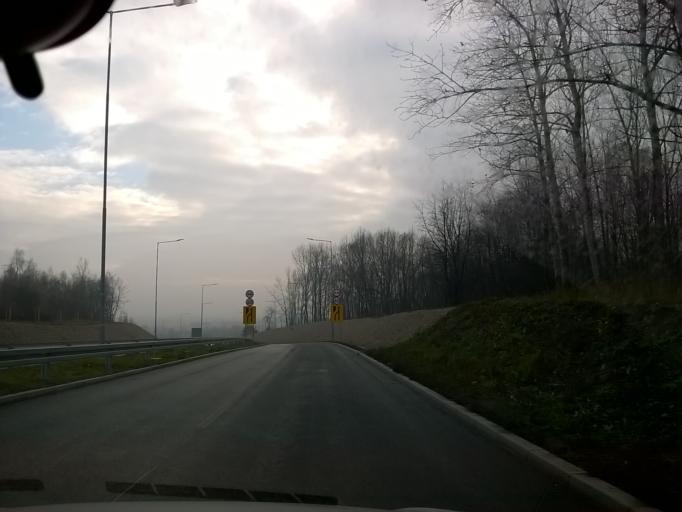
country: PL
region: Silesian Voivodeship
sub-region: Ruda Slaska
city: Ruda Slaska
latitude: 50.2793
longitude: 18.8458
